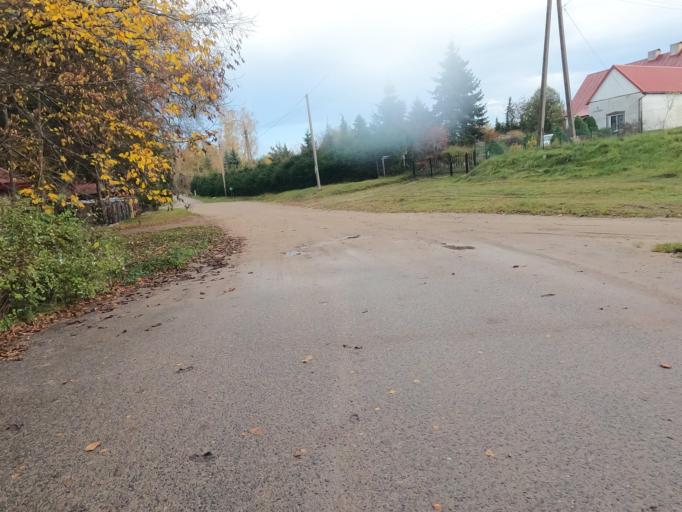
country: PL
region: West Pomeranian Voivodeship
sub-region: Powiat szczecinecki
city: Lubowo
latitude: 53.5387
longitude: 16.4415
